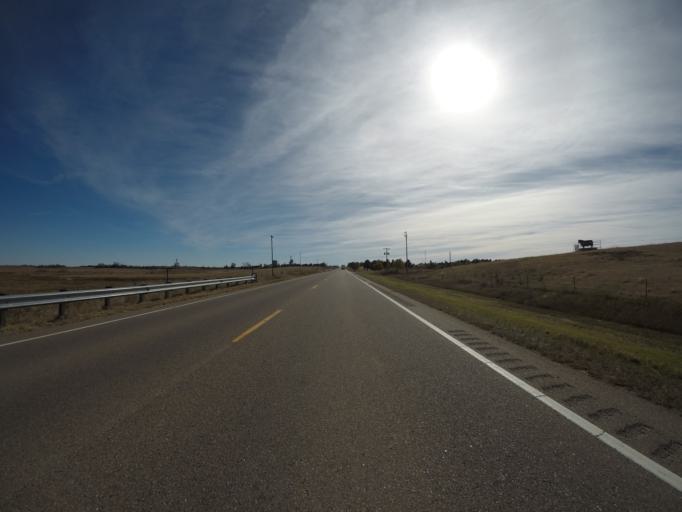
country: US
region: Colorado
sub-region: Kit Carson County
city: Burlington
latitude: 39.3383
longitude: -102.2599
